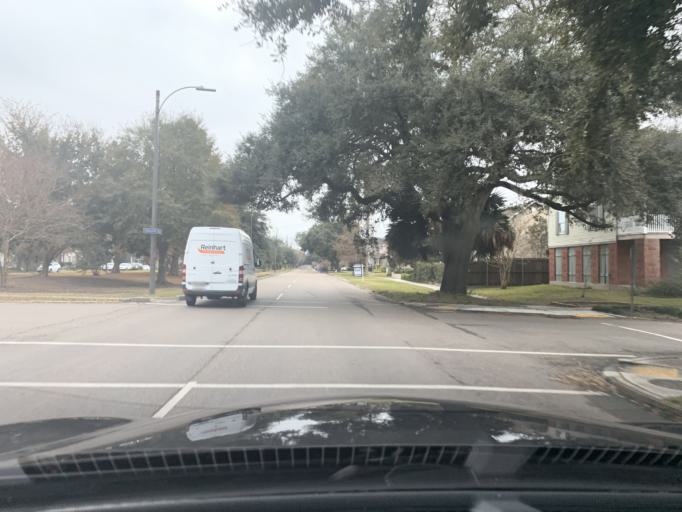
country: US
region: Louisiana
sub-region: Jefferson Parish
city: Metairie
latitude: 30.0143
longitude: -90.1071
